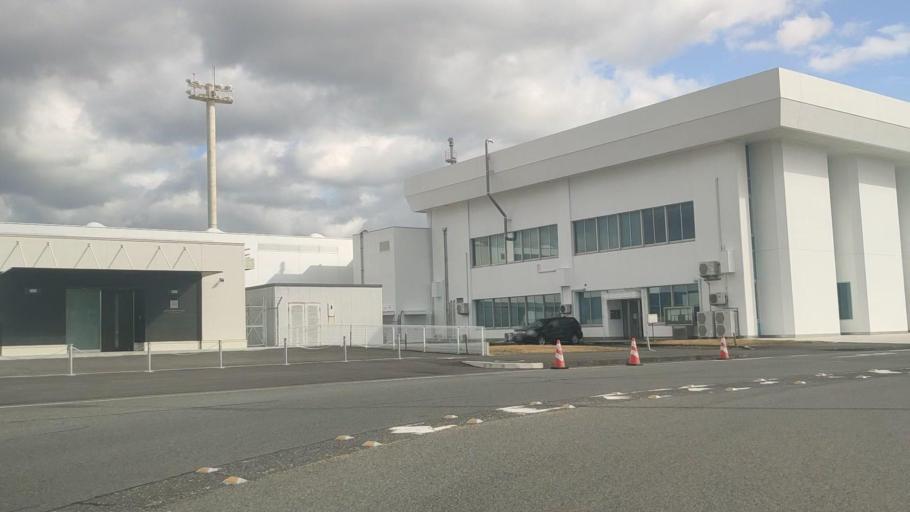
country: JP
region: Kagoshima
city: Kajiki
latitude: 31.8037
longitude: 130.7157
